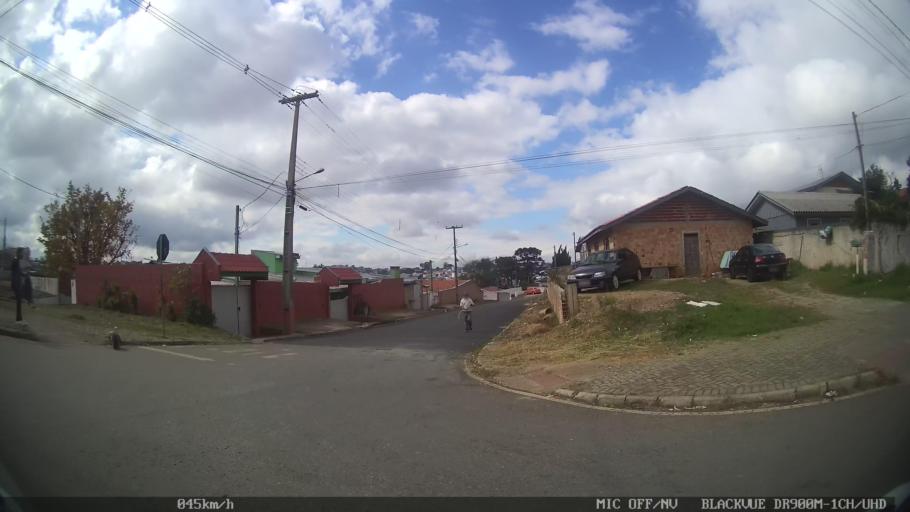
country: BR
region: Parana
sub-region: Pinhais
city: Pinhais
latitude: -25.3761
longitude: -49.2004
